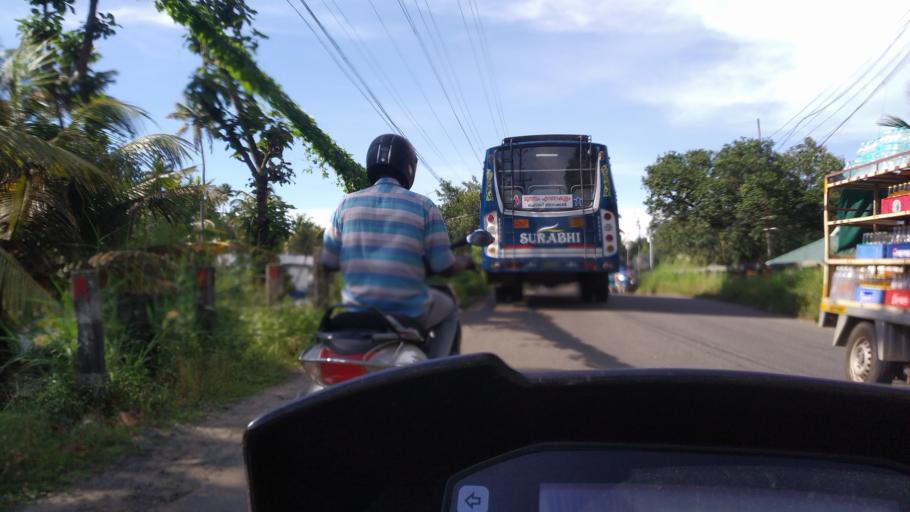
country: IN
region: Kerala
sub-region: Ernakulam
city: Elur
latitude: 10.0376
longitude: 76.2199
